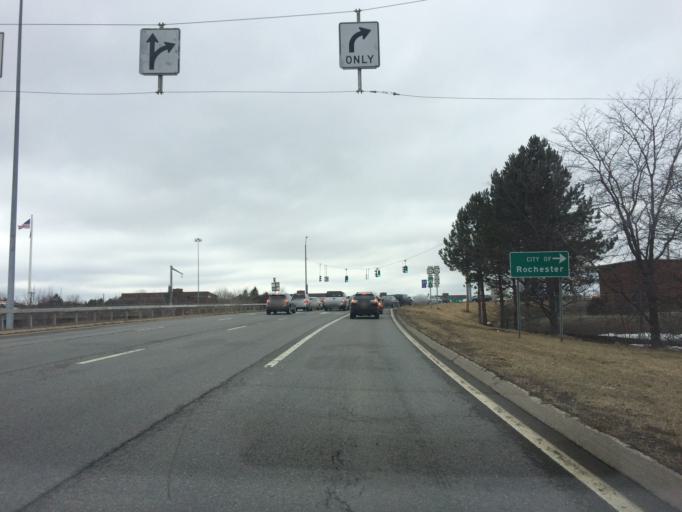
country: US
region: New York
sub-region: Monroe County
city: Rochester
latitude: 43.1083
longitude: -77.6147
